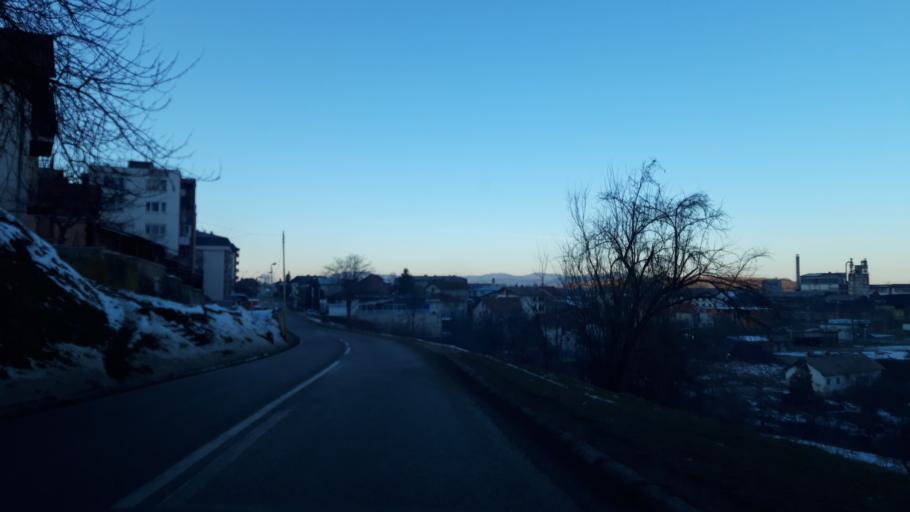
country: BA
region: Republika Srpska
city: Vlasenica
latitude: 44.1811
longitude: 18.9460
